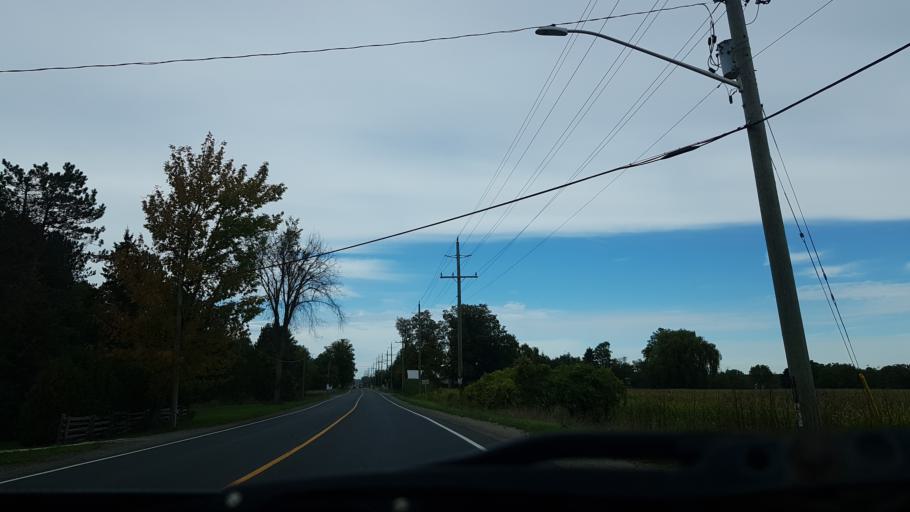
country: CA
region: Ontario
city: Angus
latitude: 44.3080
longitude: -80.0718
